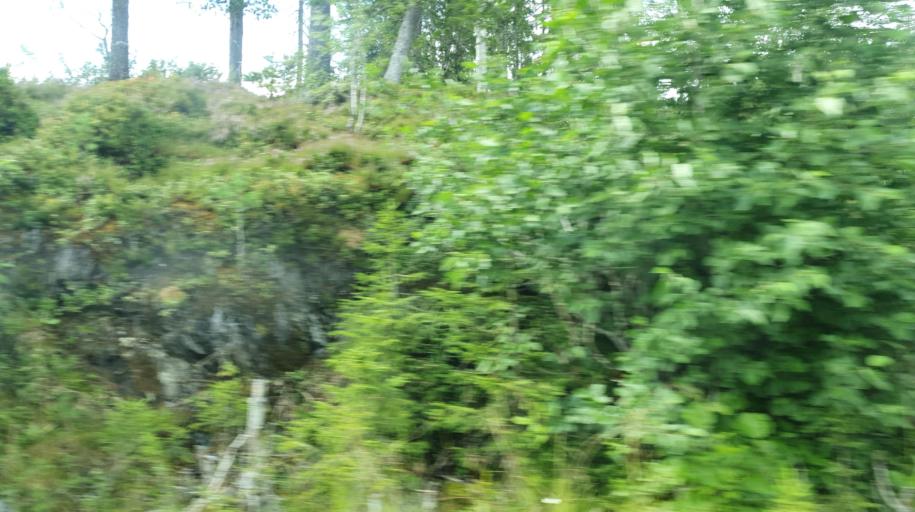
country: NO
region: Nord-Trondelag
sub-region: Levanger
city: Skogn
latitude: 63.5875
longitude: 11.2465
